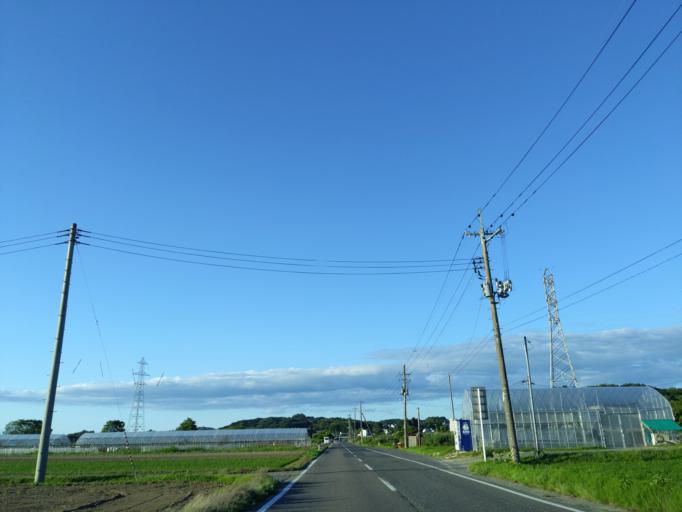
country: JP
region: Fukushima
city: Koriyama
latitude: 37.4125
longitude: 140.4125
